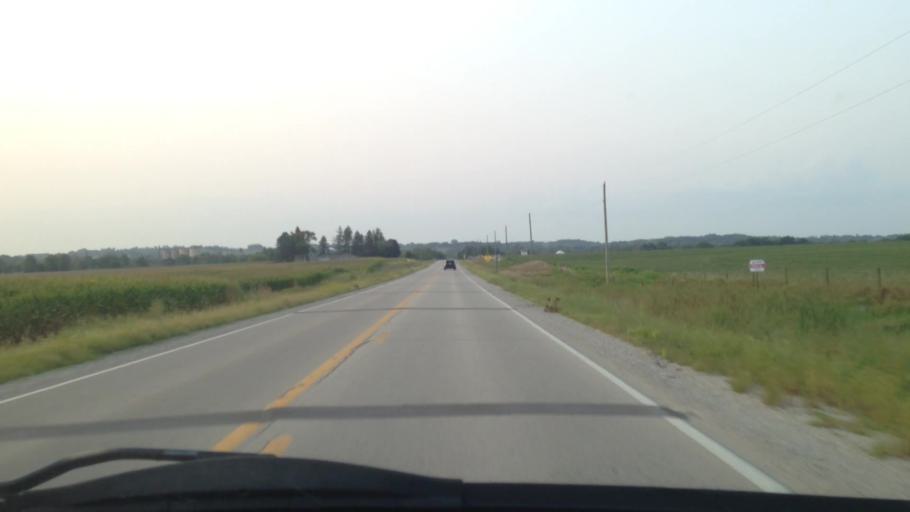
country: US
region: Iowa
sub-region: Linn County
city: Palo
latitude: 42.0811
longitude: -91.8690
